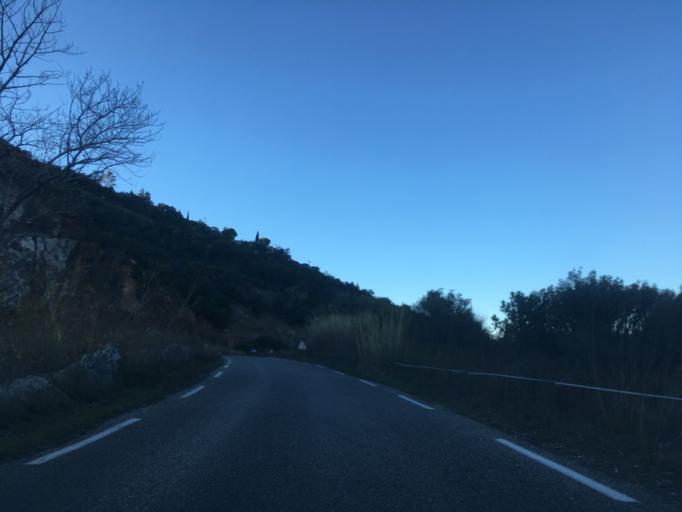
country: FR
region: Provence-Alpes-Cote d'Azur
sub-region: Departement du Var
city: Le Plan-de-la-Tour
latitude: 43.3004
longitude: 6.5580
